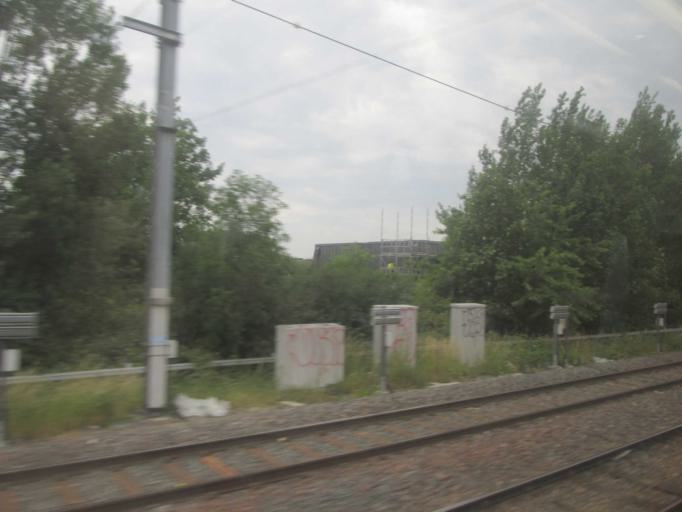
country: GB
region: England
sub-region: Greater London
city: Belsize Park
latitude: 51.5551
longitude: -0.2099
